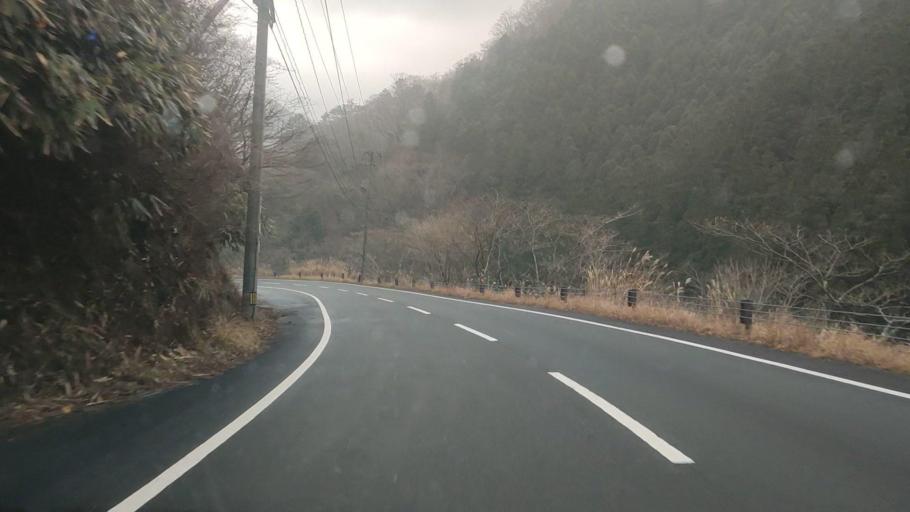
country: JP
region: Kumamoto
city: Matsubase
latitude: 32.5500
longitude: 130.9345
